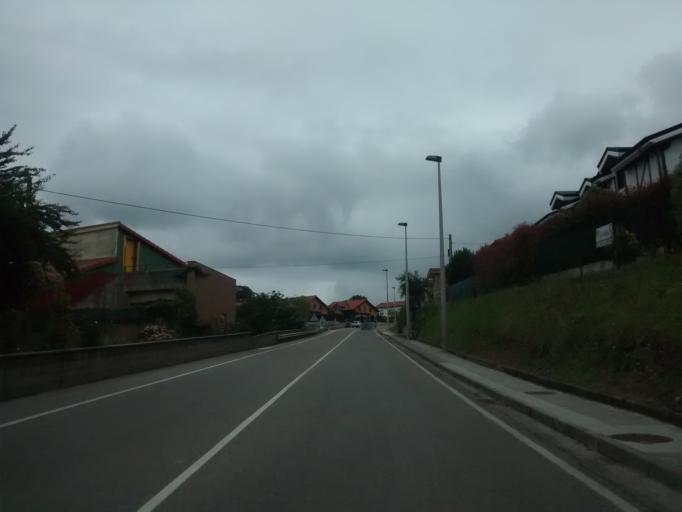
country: ES
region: Cantabria
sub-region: Provincia de Cantabria
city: Polanco
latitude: 43.3904
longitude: -4.0473
